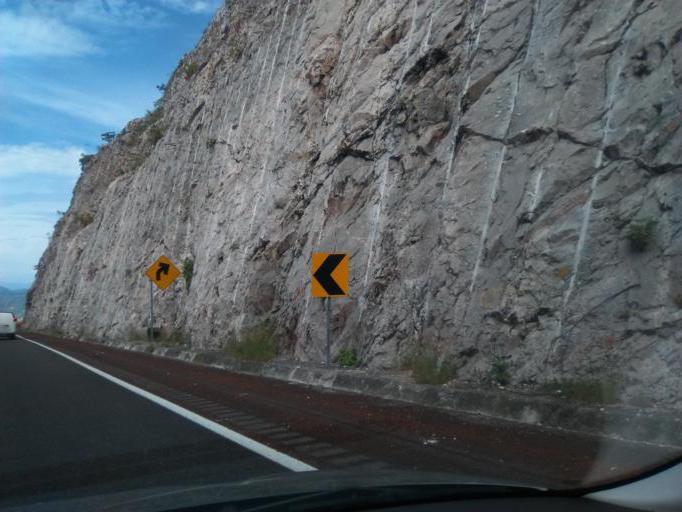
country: MX
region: Guerrero
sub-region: Eduardo Neri
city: Tlanipatla
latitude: 17.8592
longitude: -99.4056
